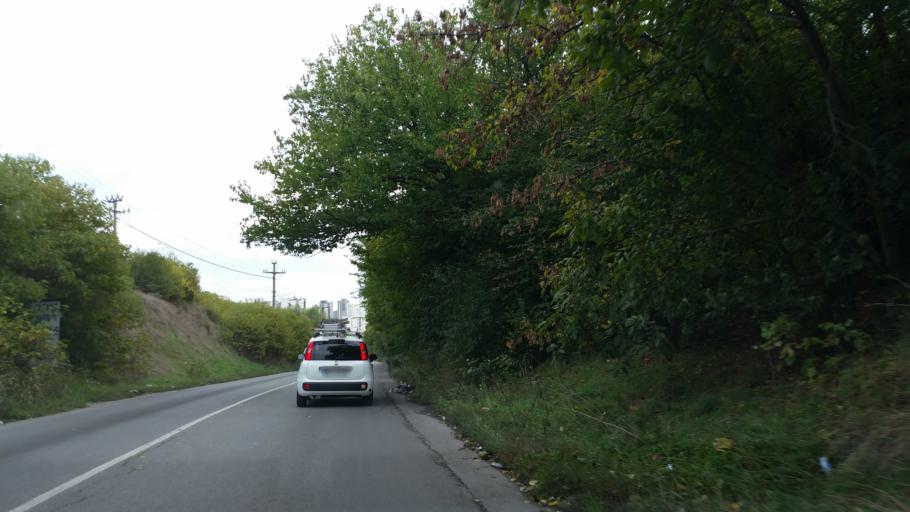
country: RS
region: Central Serbia
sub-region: Belgrade
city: Zemun
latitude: 44.8071
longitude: 20.3619
